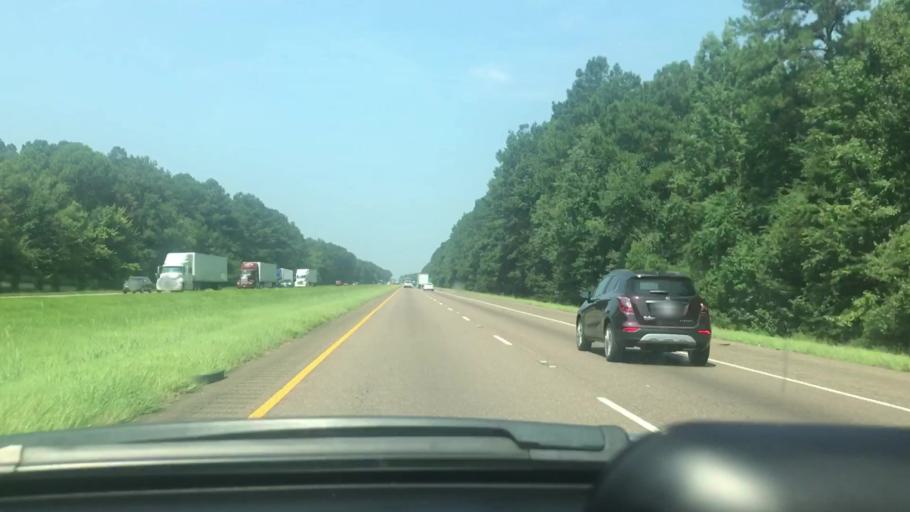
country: US
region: Louisiana
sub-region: Livingston Parish
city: Livingston
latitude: 30.4742
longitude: -90.7701
